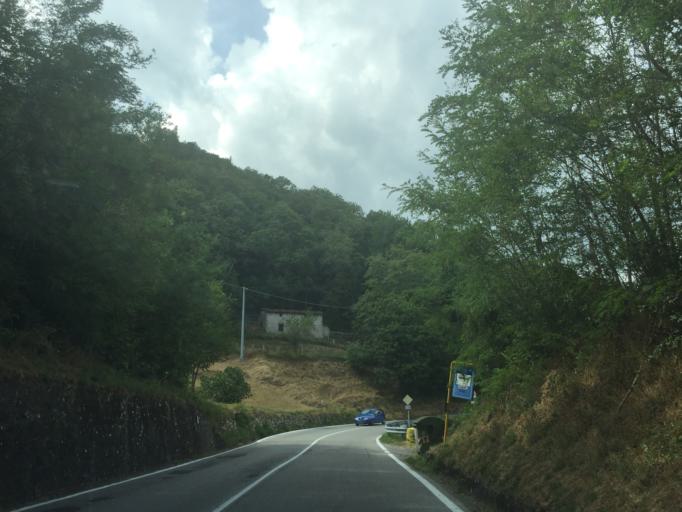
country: IT
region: Tuscany
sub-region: Provincia di Pistoia
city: Cutigliano
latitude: 44.1045
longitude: 10.7417
